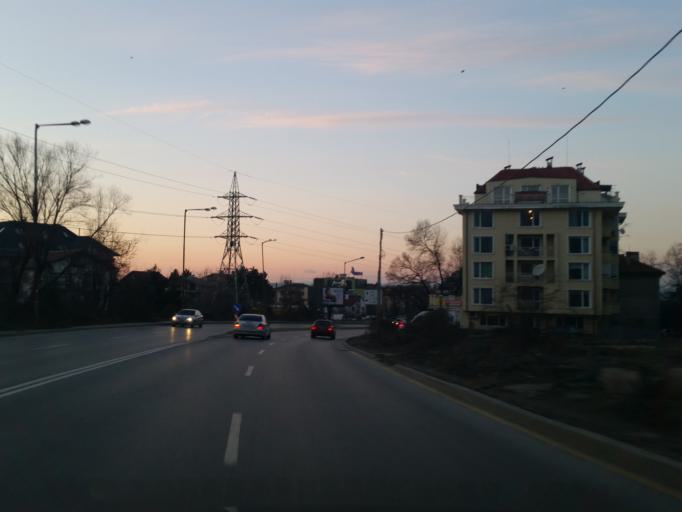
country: BG
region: Sofia-Capital
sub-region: Stolichna Obshtina
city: Sofia
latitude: 42.6440
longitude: 23.3340
